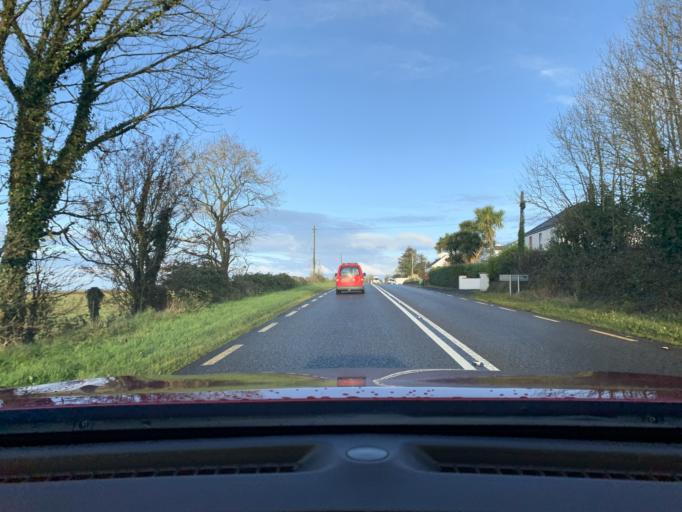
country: IE
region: Connaught
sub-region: Sligo
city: Sligo
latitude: 54.3563
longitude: -8.5172
